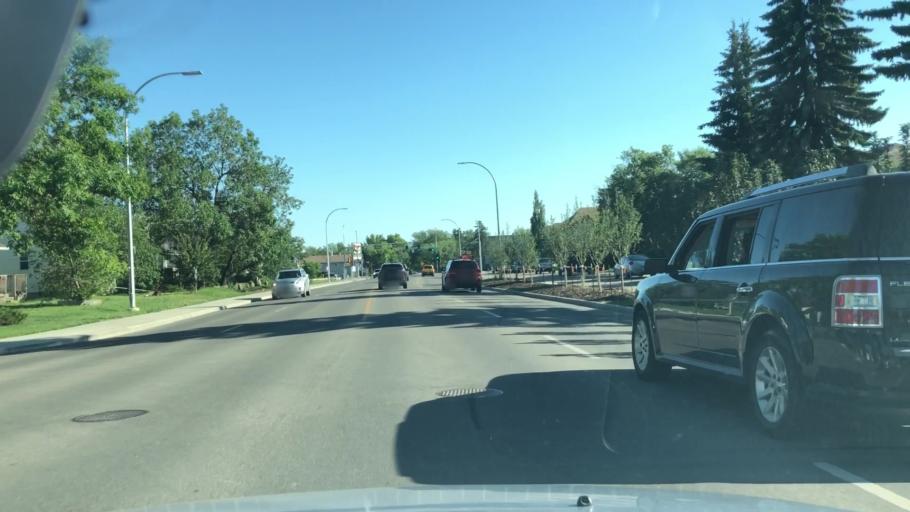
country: CA
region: Alberta
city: Edmonton
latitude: 53.5720
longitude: -113.5412
